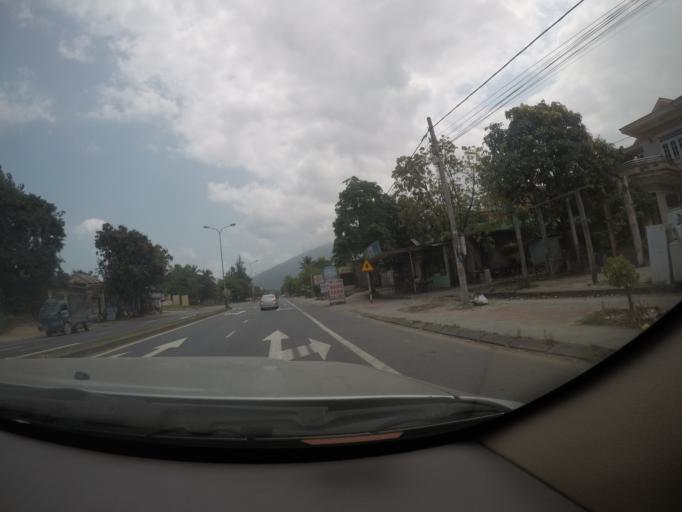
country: VN
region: Da Nang
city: Lien Chieu
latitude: 16.2448
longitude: 108.0759
